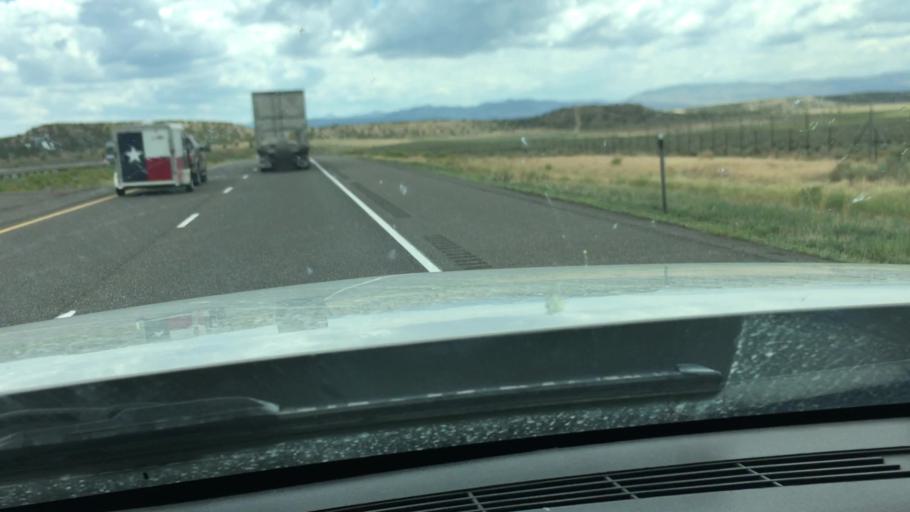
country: US
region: Utah
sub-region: Beaver County
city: Beaver
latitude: 38.3462
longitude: -112.6594
